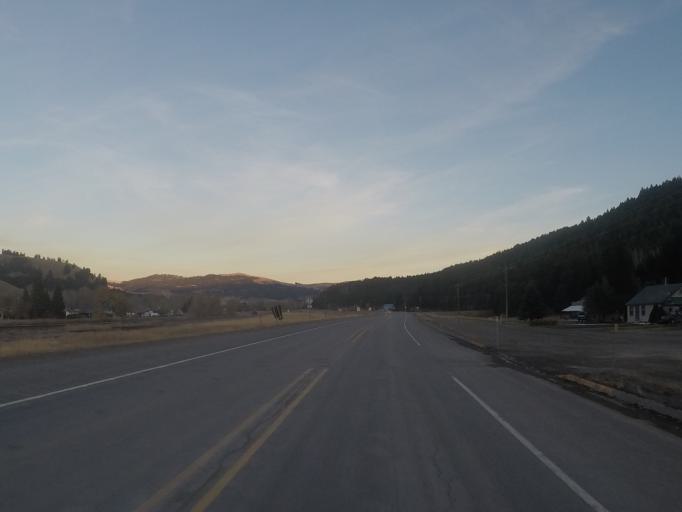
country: US
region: Montana
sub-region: Lewis and Clark County
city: Helena West Side
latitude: 46.5614
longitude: -112.4312
